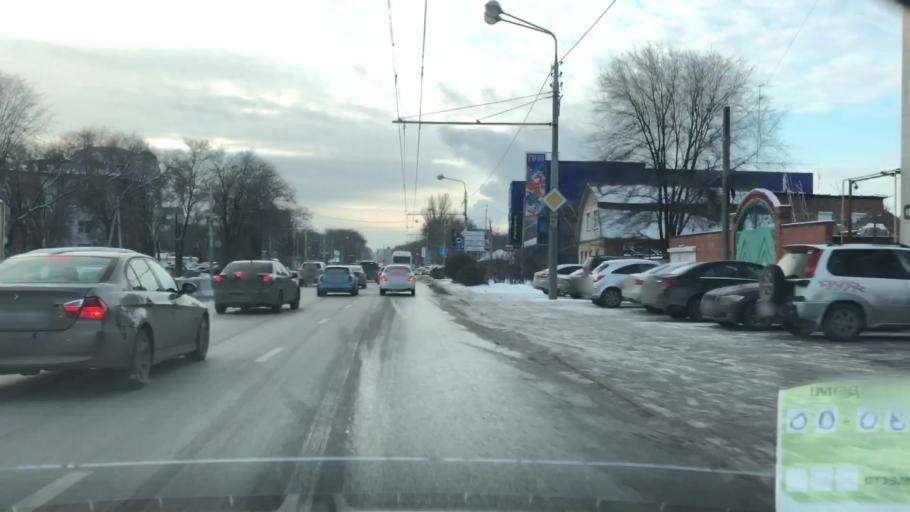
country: RU
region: Rostov
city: Rostov-na-Donu
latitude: 47.2122
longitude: 39.6501
